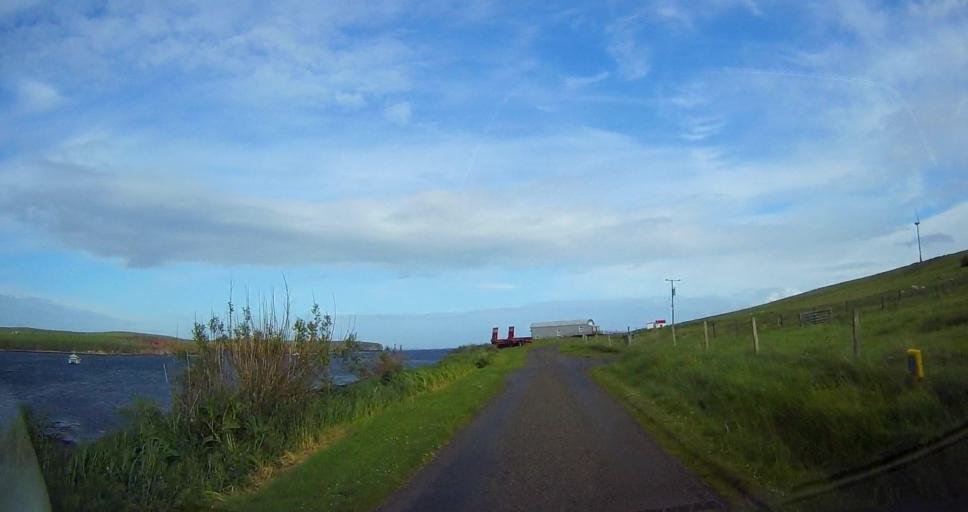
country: GB
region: Scotland
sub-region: Orkney Islands
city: Stromness
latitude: 58.7805
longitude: -3.2312
